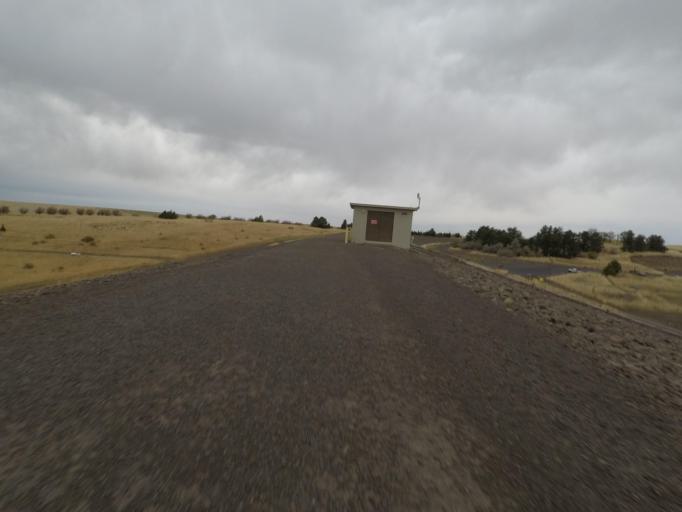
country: US
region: Washington
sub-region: Walla Walla County
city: Walla Walla East
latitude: 46.0641
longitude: -118.2637
